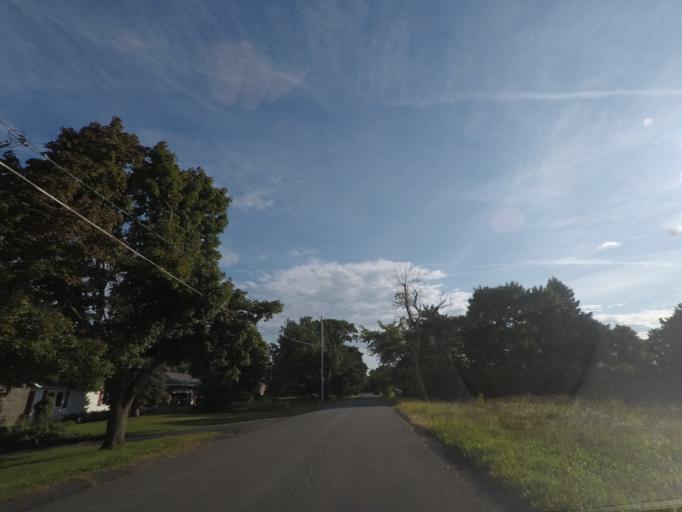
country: US
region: New York
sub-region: Rensselaer County
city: Hampton Manor
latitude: 42.6350
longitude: -73.6998
